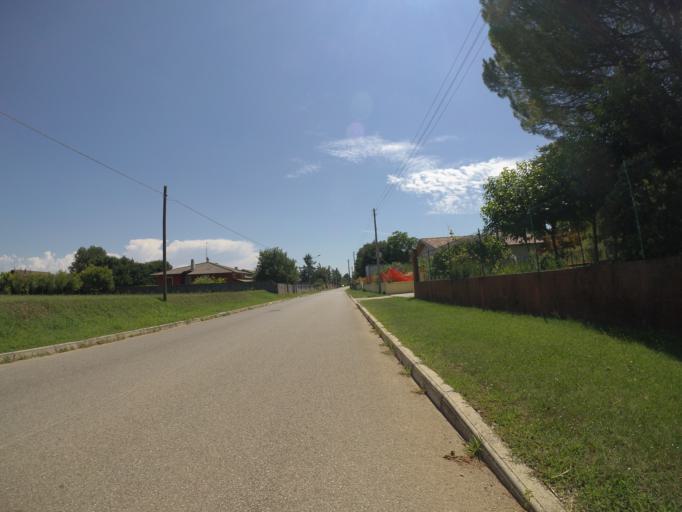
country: IT
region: Friuli Venezia Giulia
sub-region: Provincia di Udine
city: Talmassons
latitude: 45.9347
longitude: 13.1159
